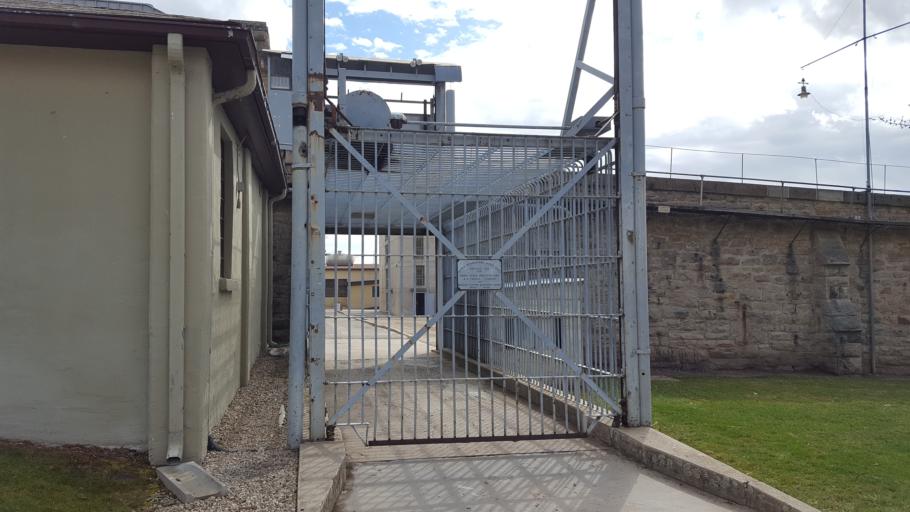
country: US
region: Idaho
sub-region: Ada County
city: Boise
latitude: 43.6033
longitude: -116.1625
